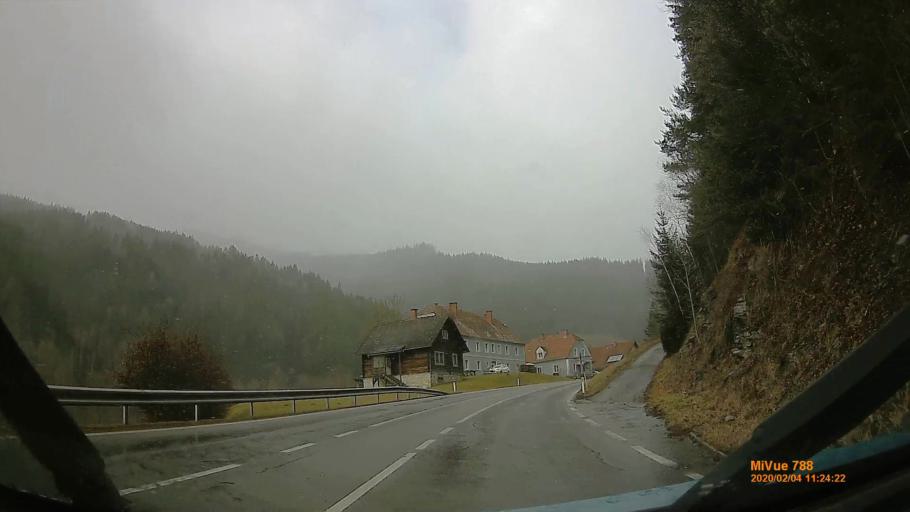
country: AT
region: Styria
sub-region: Politischer Bezirk Bruck-Muerzzuschlag
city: Muerzzuschlag
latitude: 47.6245
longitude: 15.6621
